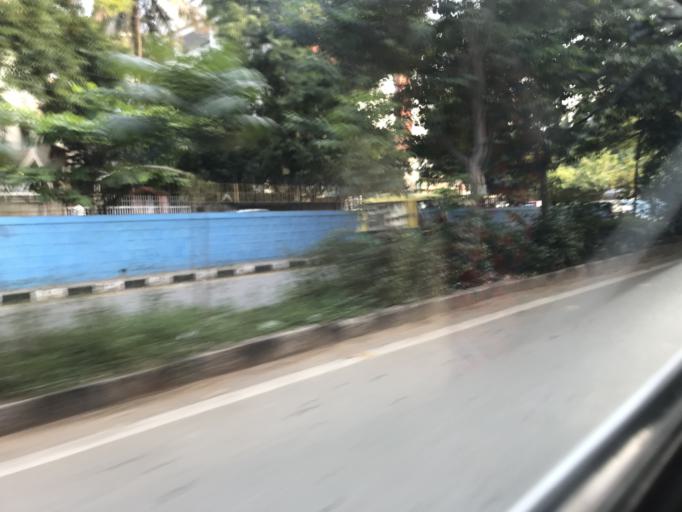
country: IN
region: Karnataka
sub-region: Bangalore Urban
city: Bangalore
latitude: 12.9950
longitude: 77.5897
